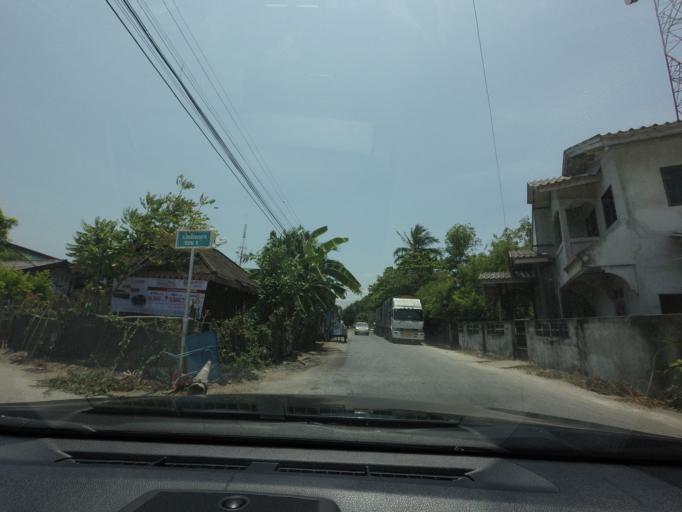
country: TH
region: Pattani
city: Yaring
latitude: 6.8627
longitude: 101.3679
